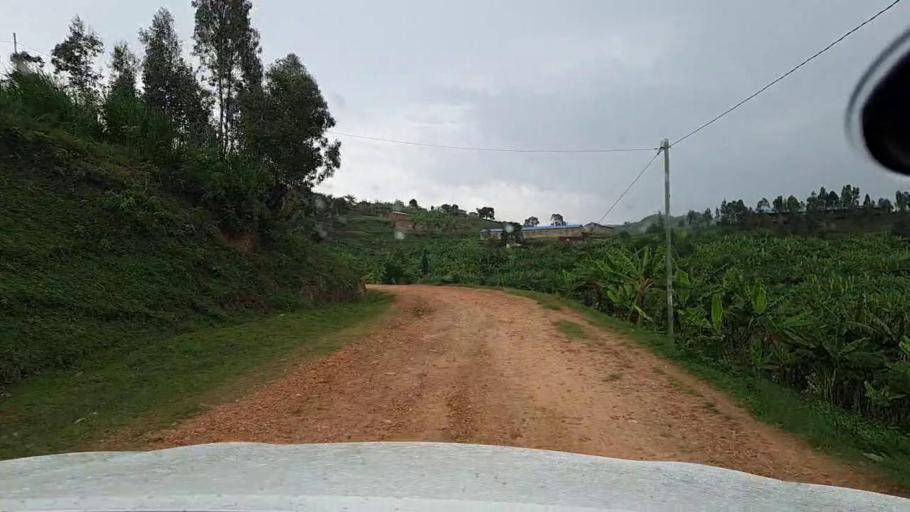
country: RW
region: Western Province
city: Kibuye
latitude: -2.0780
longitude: 29.4424
